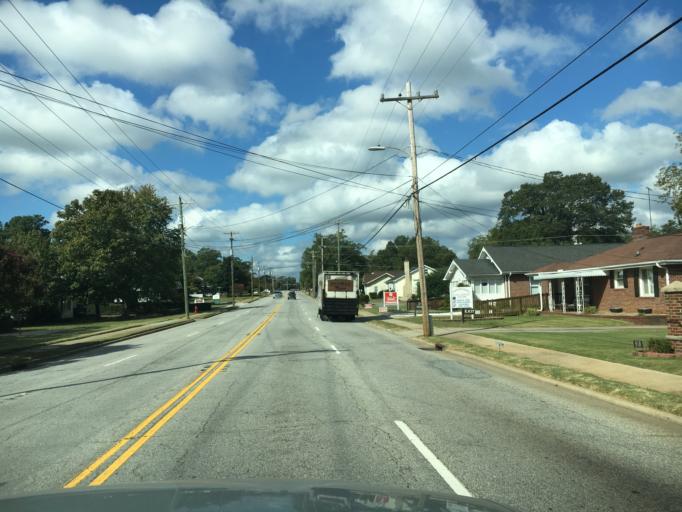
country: US
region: South Carolina
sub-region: Greenville County
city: Greer
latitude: 34.9424
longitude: -82.2415
